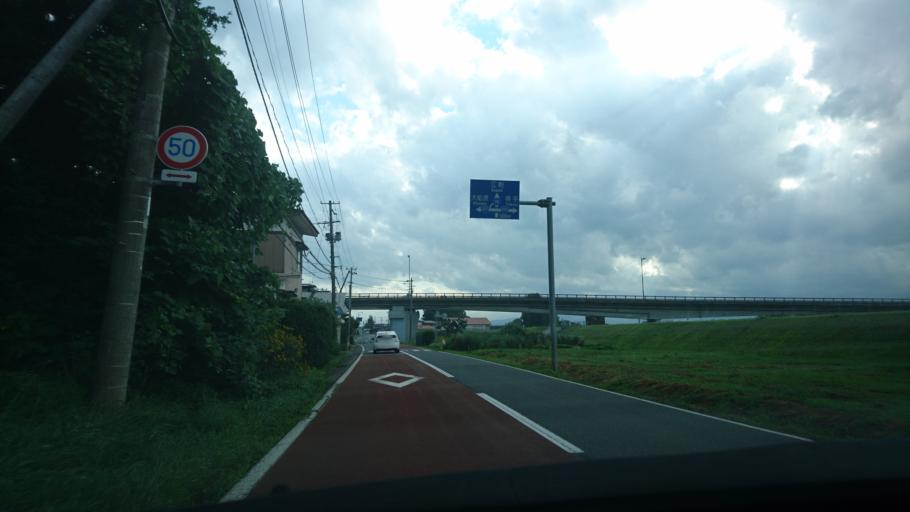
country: JP
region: Iwate
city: Kitakami
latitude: 39.2901
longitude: 141.1420
